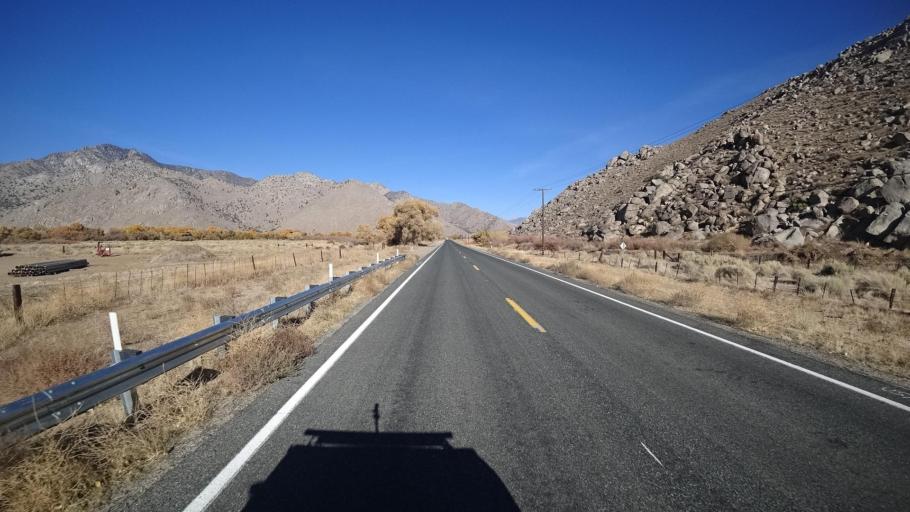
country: US
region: California
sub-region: Kern County
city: Weldon
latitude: 35.6774
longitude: -118.2539
